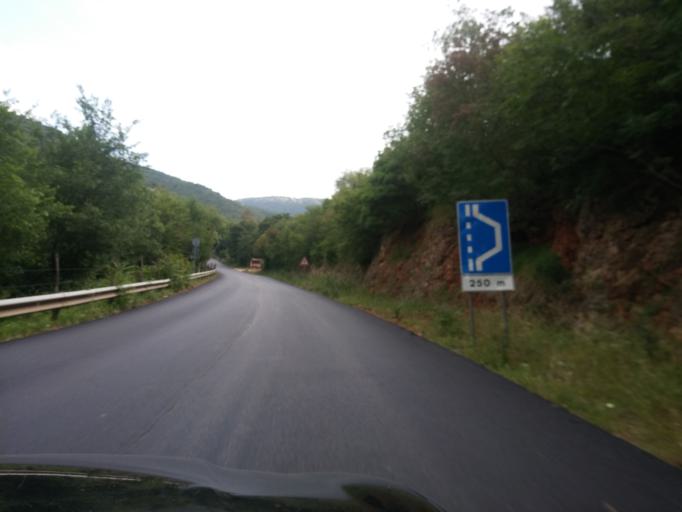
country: IT
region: Apulia
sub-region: Provincia di Foggia
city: Rignano Garganico
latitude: 41.7192
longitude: 15.5759
